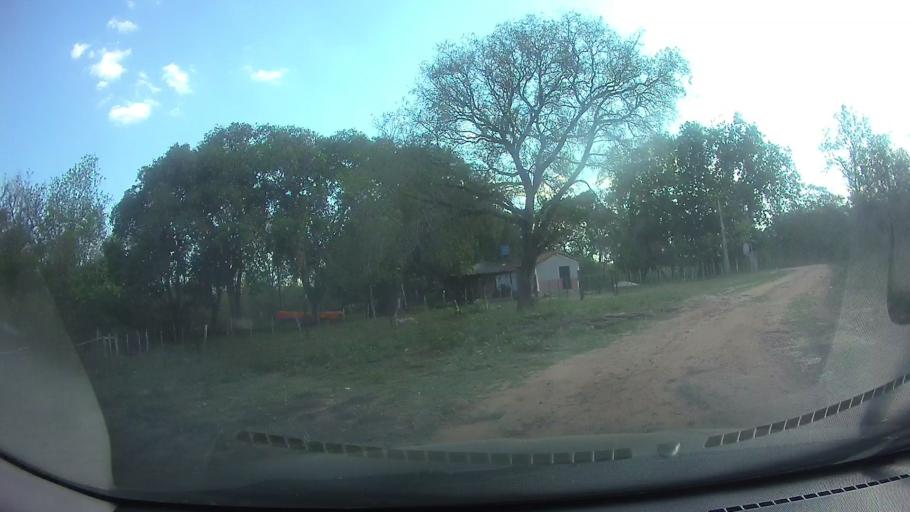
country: PY
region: Cordillera
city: Arroyos y Esteros
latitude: -24.9741
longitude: -57.1935
